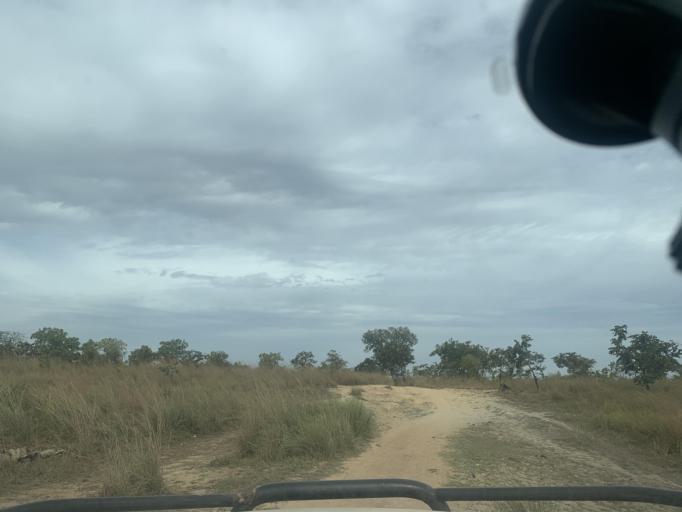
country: GN
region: Kankan
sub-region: Mandiana Prefecture
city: Mandiana
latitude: 10.9544
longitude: -8.6539
